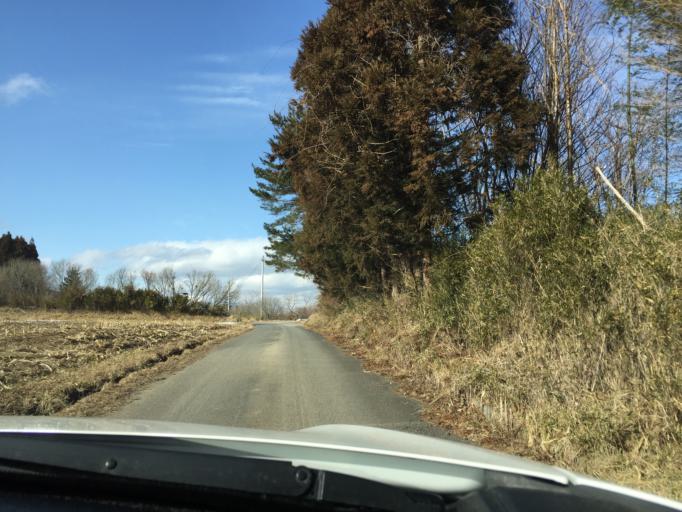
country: JP
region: Fukushima
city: Ishikawa
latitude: 37.2514
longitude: 140.5575
